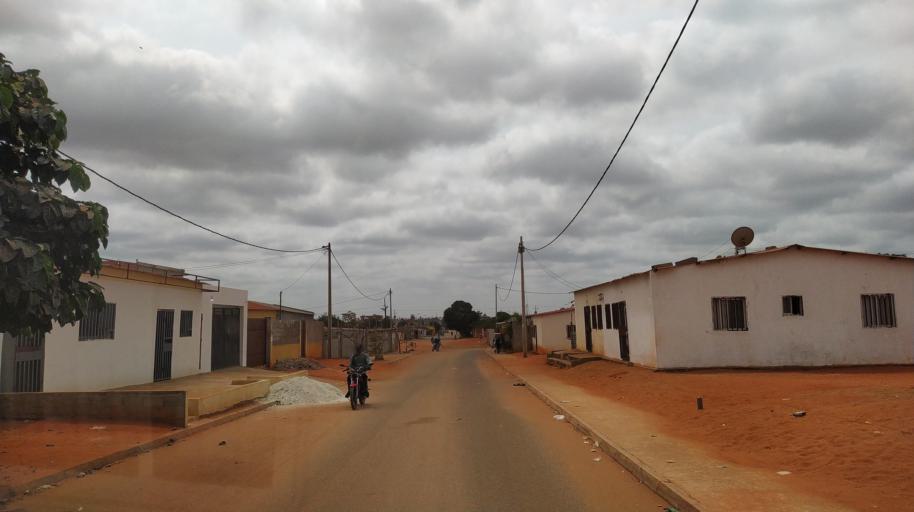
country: AO
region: Luanda
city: Luanda
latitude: -9.0709
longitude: 13.4273
